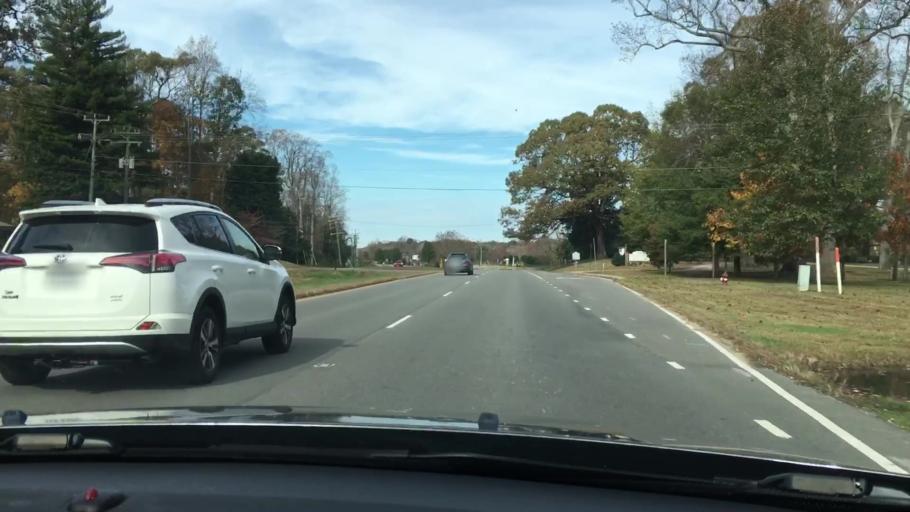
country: US
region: Virginia
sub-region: James City County
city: Williamsburg
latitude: 37.3920
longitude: -76.8042
